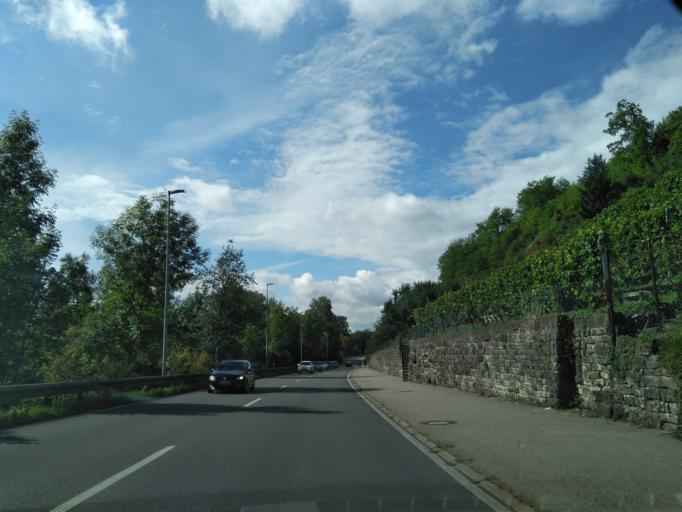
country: DE
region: Baden-Wuerttemberg
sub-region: Regierungsbezirk Stuttgart
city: Besigheim
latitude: 48.9684
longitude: 9.1416
